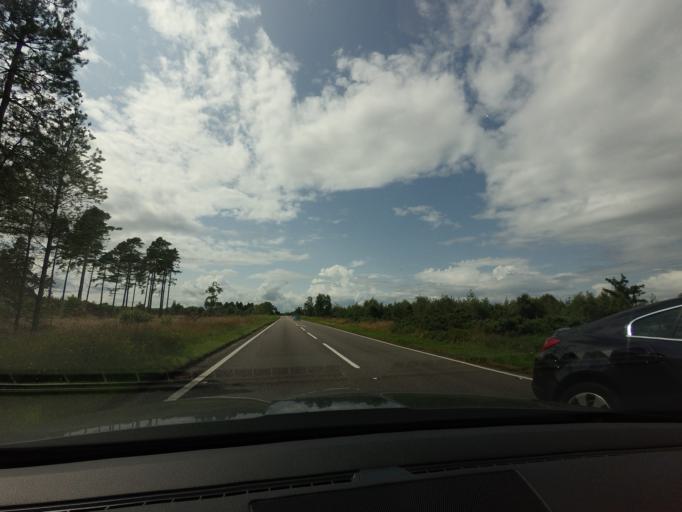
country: GB
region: Scotland
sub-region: Moray
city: Burghead
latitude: 57.6349
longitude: -3.4877
